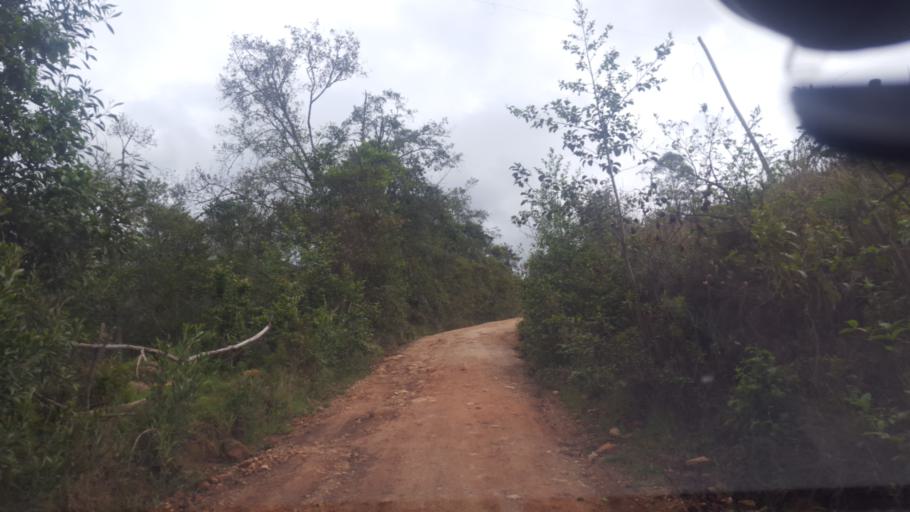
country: CO
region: Boyaca
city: Cerinza
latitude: 5.9895
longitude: -72.9494
